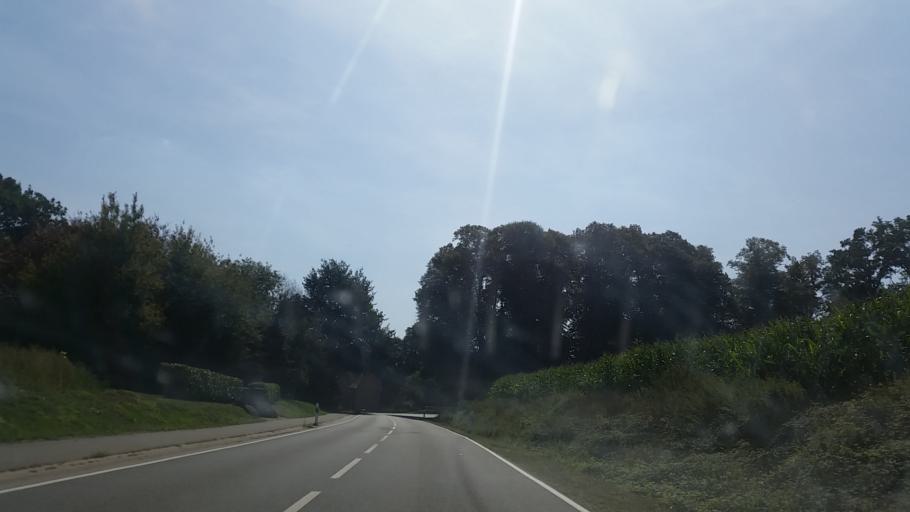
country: DE
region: Lower Saxony
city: Ankum
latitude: 52.5307
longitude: 7.8924
